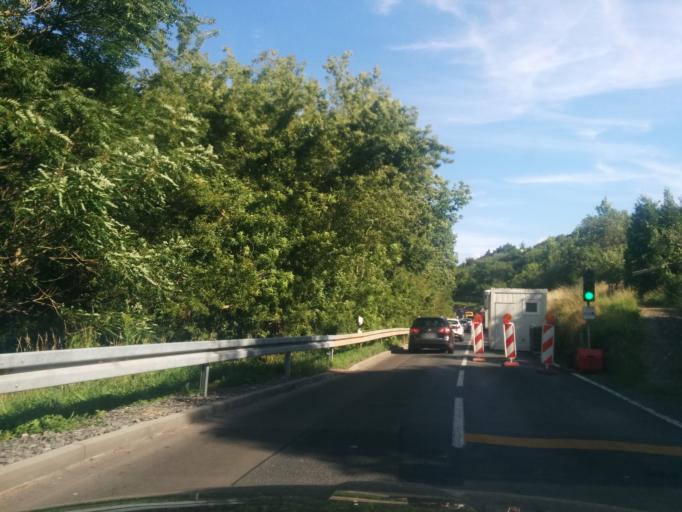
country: DE
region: Saxony-Anhalt
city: Hohnstedt
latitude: 51.4931
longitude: 11.7453
